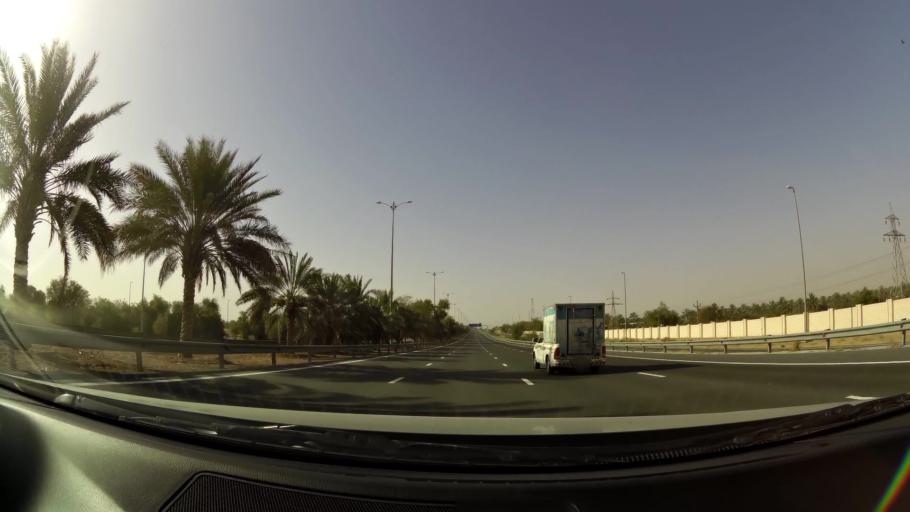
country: OM
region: Al Buraimi
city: Al Buraymi
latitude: 24.4257
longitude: 55.7894
